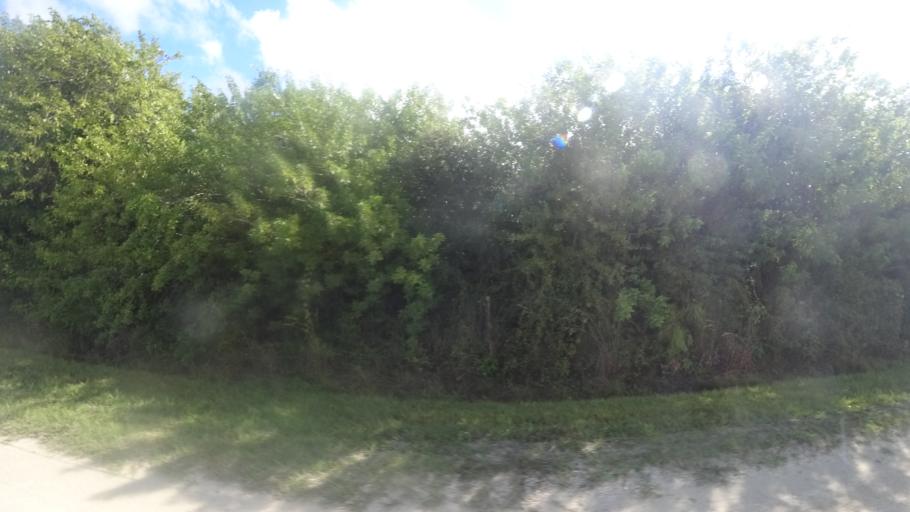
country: US
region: Florida
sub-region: Hillsborough County
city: Ruskin
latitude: 27.6357
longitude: -82.4171
